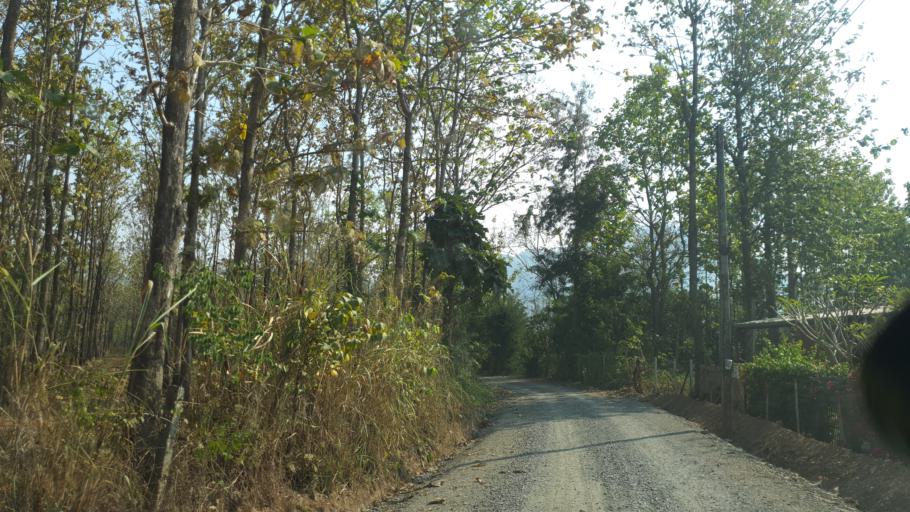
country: TH
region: Chiang Mai
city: Mae On
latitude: 18.7483
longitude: 99.2491
